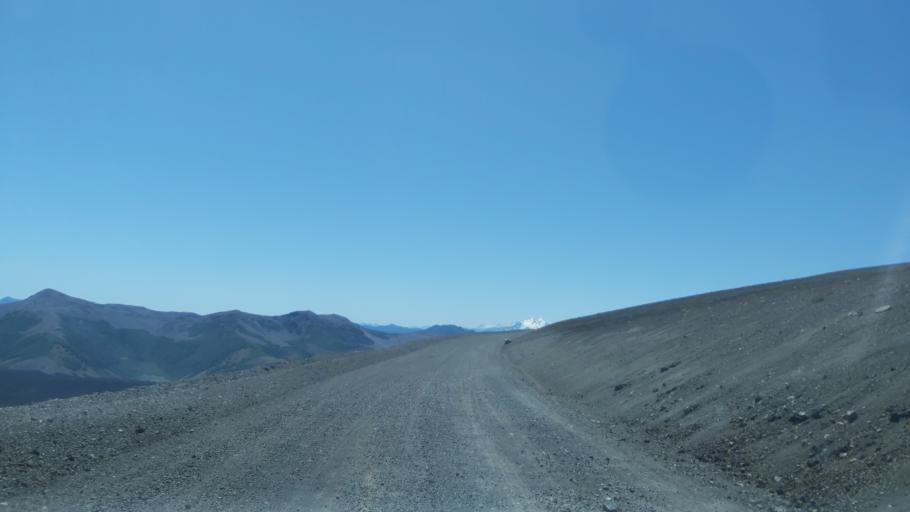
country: CL
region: Araucania
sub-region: Provincia de Cautin
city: Vilcun
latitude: -38.3691
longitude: -71.5400
